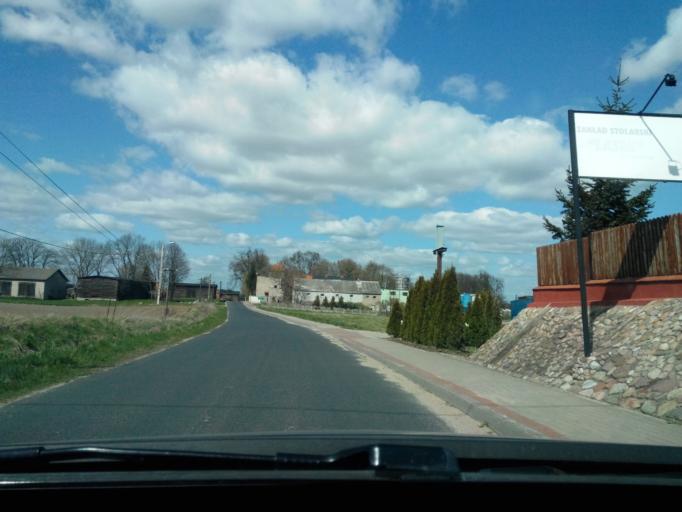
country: PL
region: Warmian-Masurian Voivodeship
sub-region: Powiat nowomiejski
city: Biskupiec
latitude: 53.4672
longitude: 19.3189
